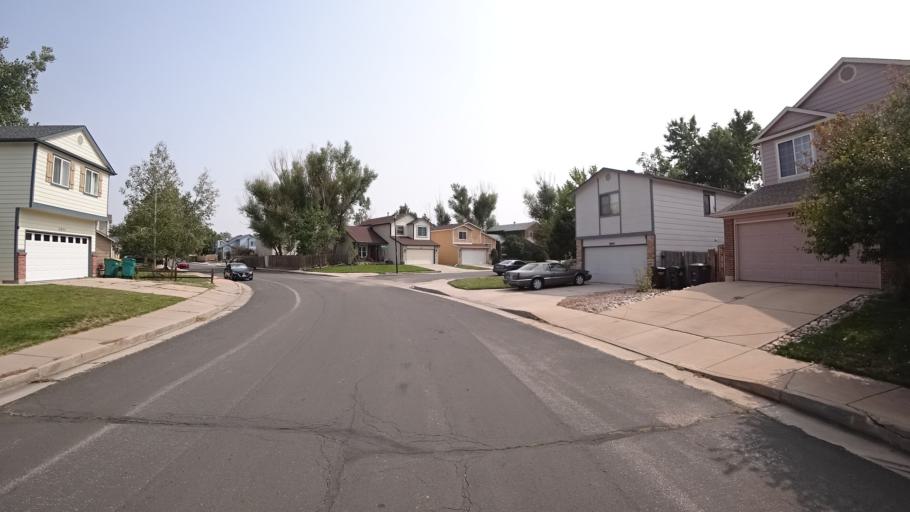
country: US
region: Colorado
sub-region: El Paso County
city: Cimarron Hills
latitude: 38.9201
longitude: -104.7280
